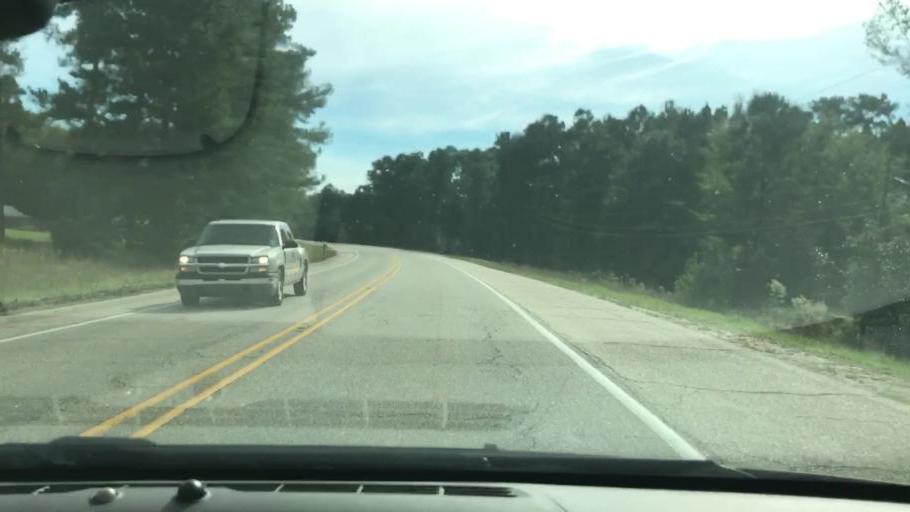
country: US
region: Louisiana
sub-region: Saint Tammany Parish
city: Pearl River
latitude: 30.4464
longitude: -89.7980
